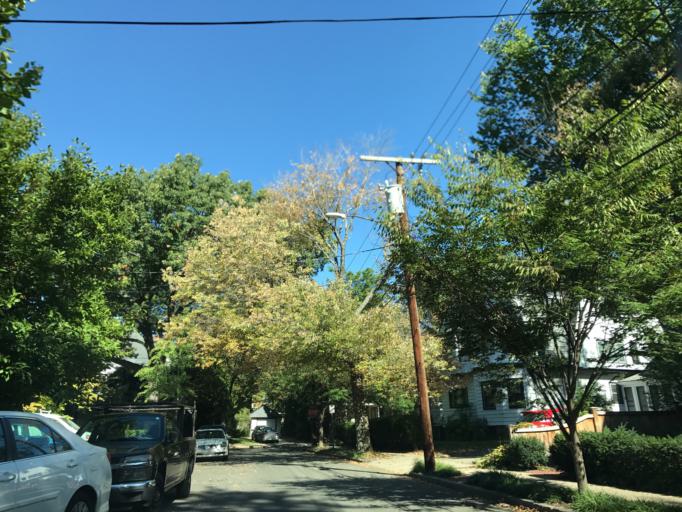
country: US
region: Massachusetts
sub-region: Norfolk County
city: Brookline
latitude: 42.3480
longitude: -71.1225
